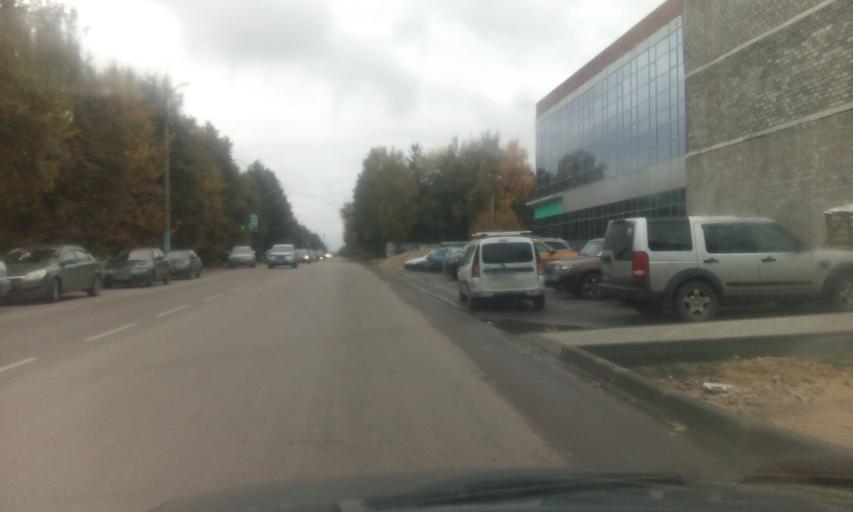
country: RU
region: Tula
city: Uzlovaya
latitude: 53.9803
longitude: 38.1573
